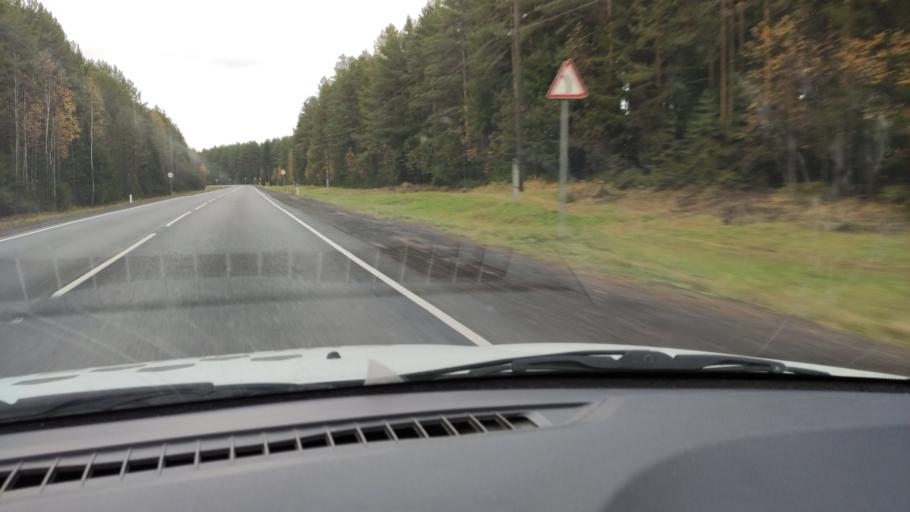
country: RU
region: Kirov
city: Belaya Kholunitsa
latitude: 58.8774
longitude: 50.8664
